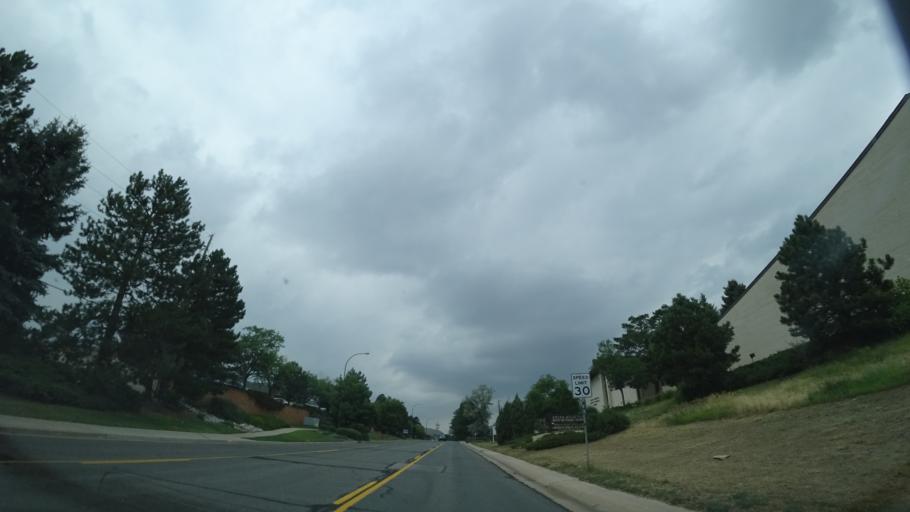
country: US
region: Colorado
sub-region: Jefferson County
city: West Pleasant View
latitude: 39.7122
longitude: -105.1414
